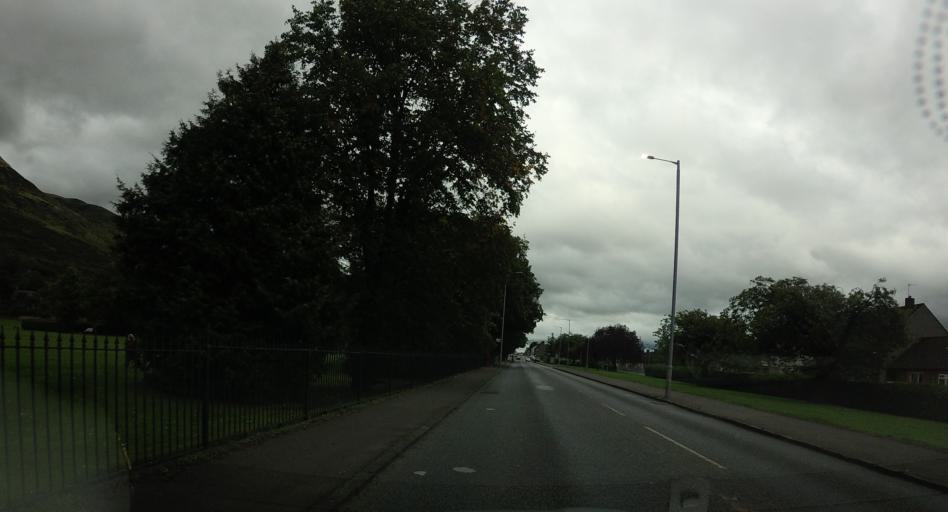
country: GB
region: Scotland
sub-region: Clackmannanshire
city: Alva
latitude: 56.1528
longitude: -3.8116
